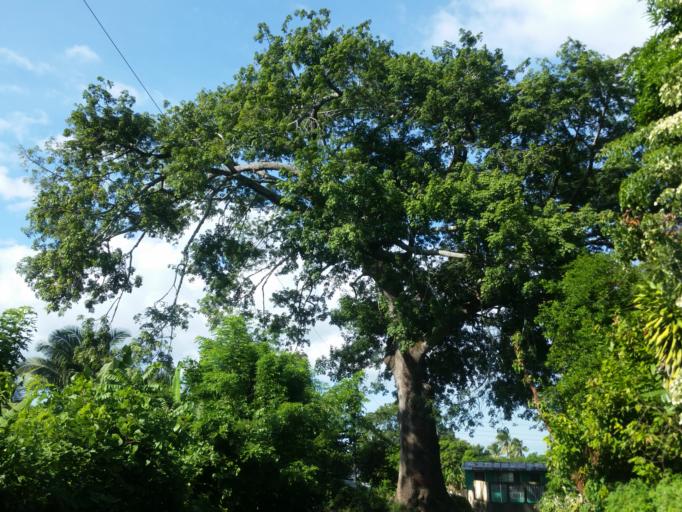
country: NI
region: Masaya
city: Catarina
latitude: 11.9358
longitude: -86.0721
